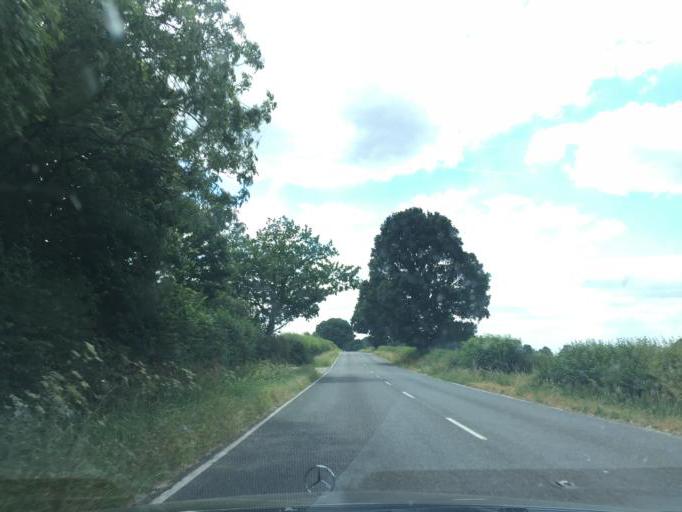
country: GB
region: England
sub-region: Leicestershire
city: Hinckley
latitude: 52.4708
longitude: -1.3821
